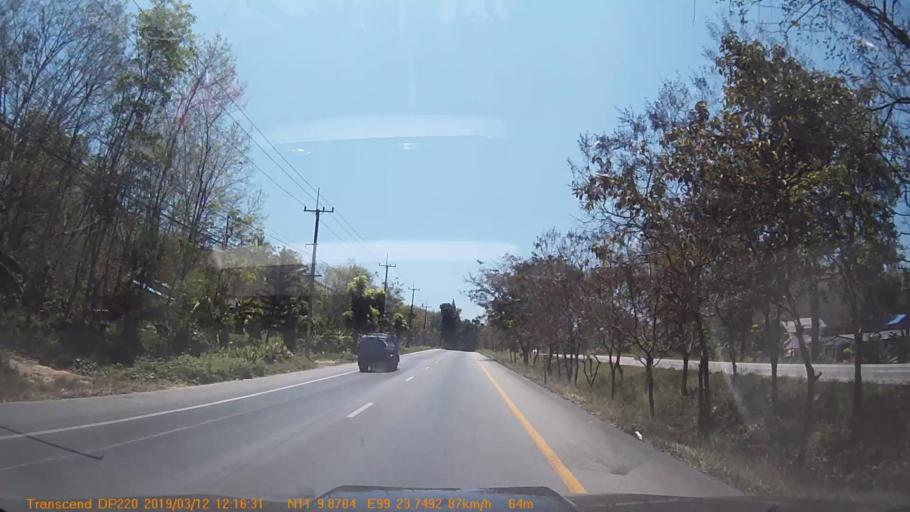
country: TH
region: Prachuap Khiri Khan
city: Bang Saphan Noi
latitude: 11.1643
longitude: 99.3958
